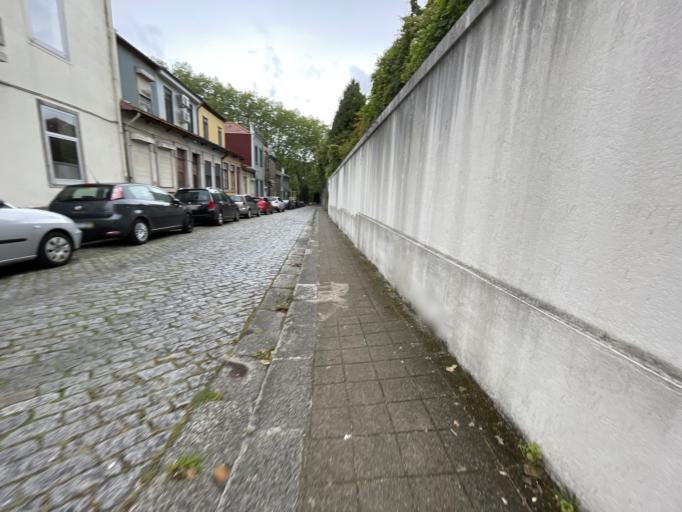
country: PT
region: Porto
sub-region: Porto
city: Porto
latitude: 41.1712
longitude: -8.6102
